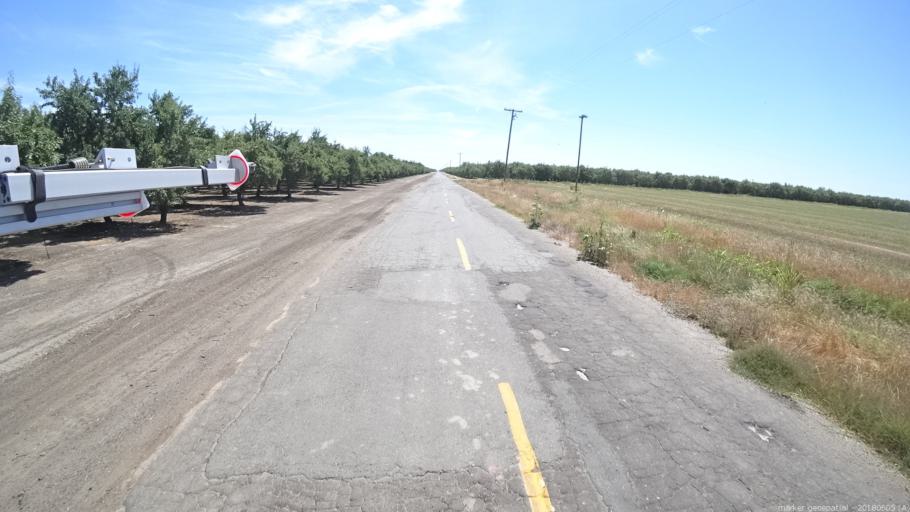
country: US
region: California
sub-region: Madera County
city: Chowchilla
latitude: 37.0983
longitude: -120.4242
